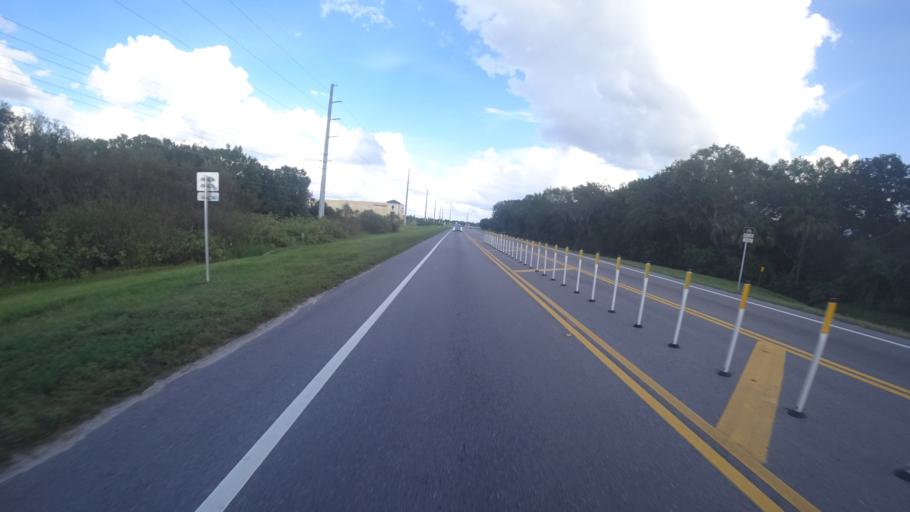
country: US
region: Florida
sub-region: Sarasota County
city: The Meadows
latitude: 27.4320
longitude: -82.3916
